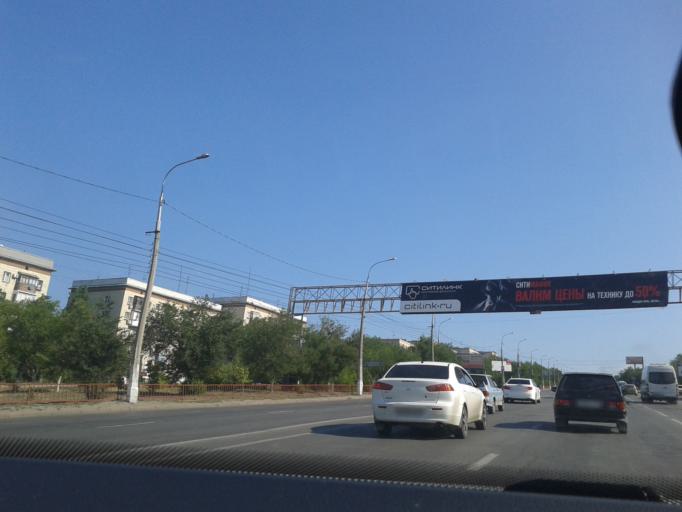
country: RU
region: Volgograd
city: Volgograd
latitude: 48.6636
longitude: 44.4399
